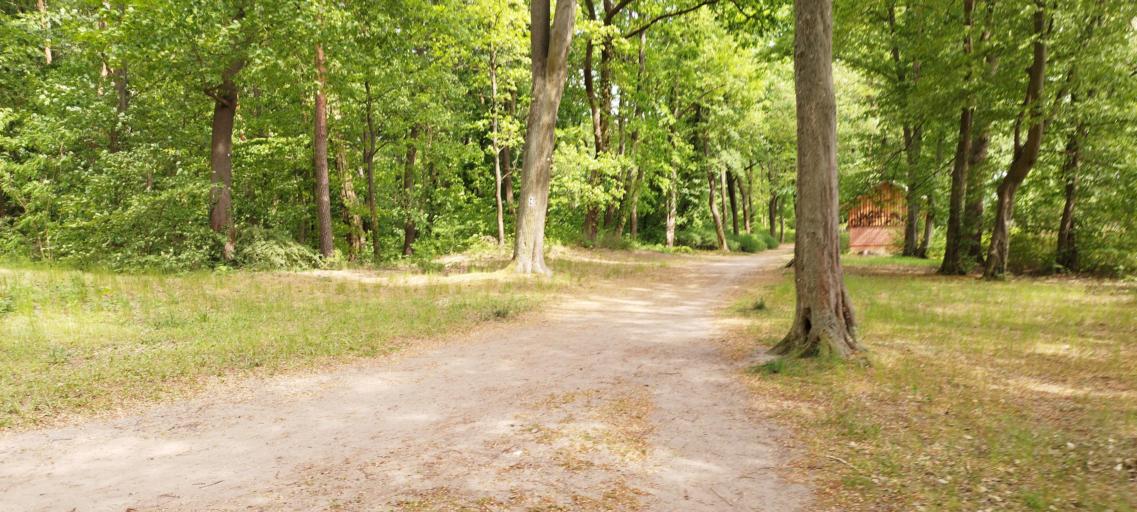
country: DE
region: Brandenburg
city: Furstenwalde
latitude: 52.3648
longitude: 14.0529
